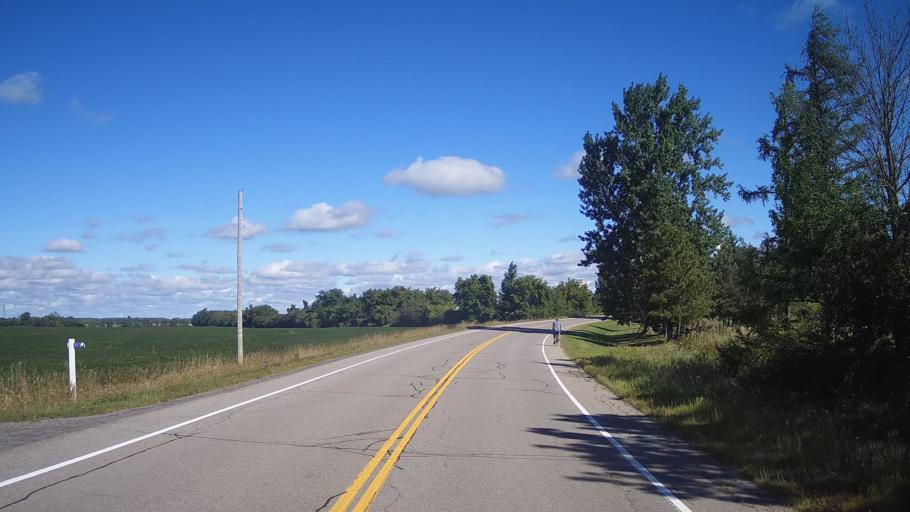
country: US
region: New York
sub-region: St. Lawrence County
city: Norfolk
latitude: 44.9590
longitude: -75.2830
